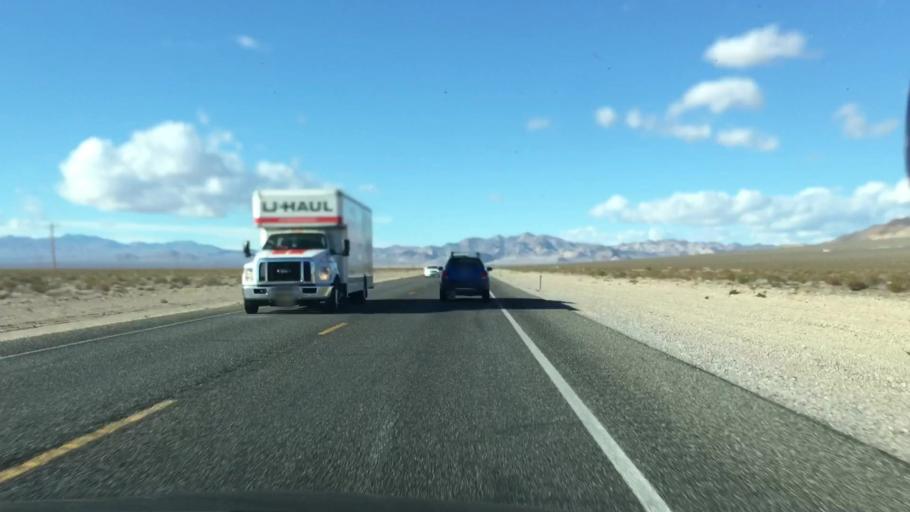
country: US
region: Nevada
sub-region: Nye County
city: Beatty
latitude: 36.7921
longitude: -116.7070
